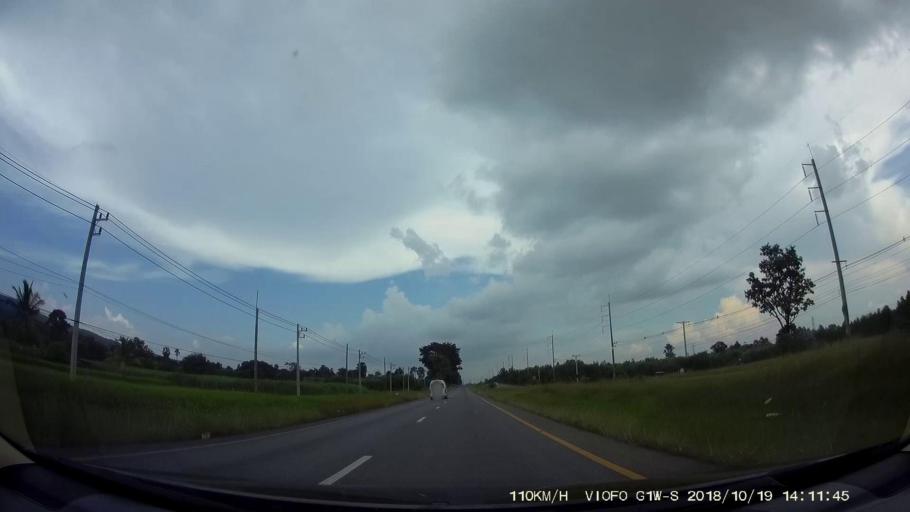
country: TH
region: Chaiyaphum
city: Khon Sawan
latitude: 15.9416
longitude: 102.1647
